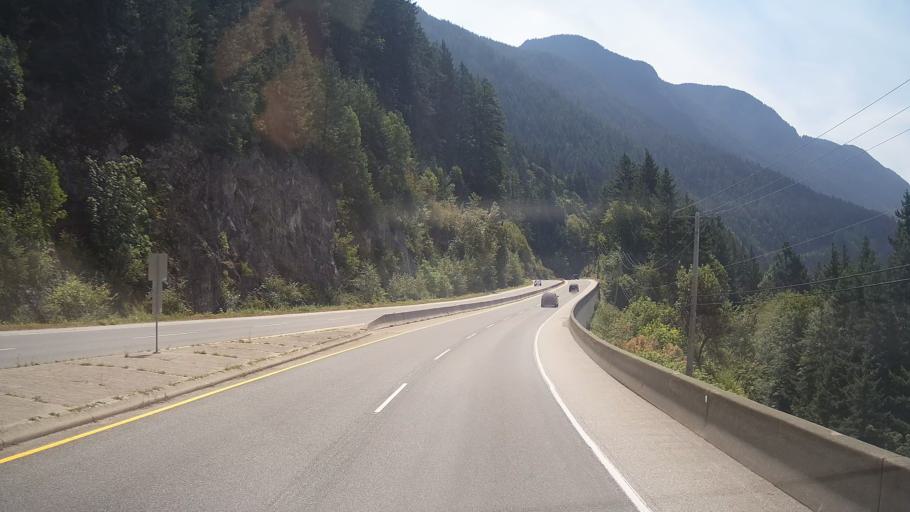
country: CA
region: British Columbia
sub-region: Greater Vancouver Regional District
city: Lions Bay
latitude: 49.4289
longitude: -123.2332
